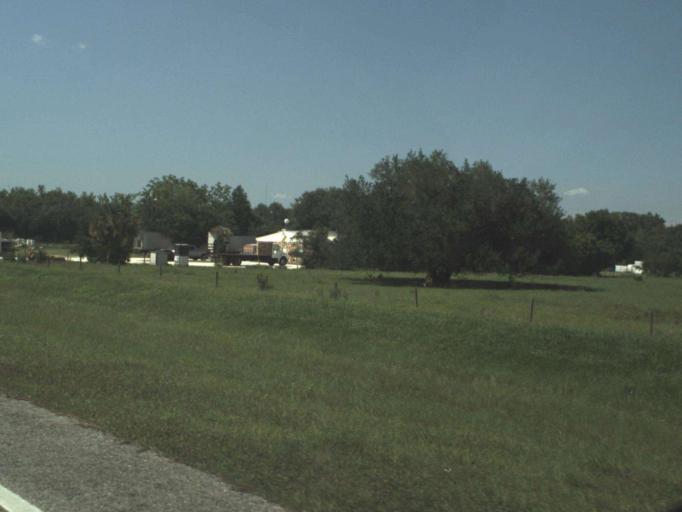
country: US
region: Florida
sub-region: Orange County
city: Wedgefield
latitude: 28.4982
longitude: -81.0477
